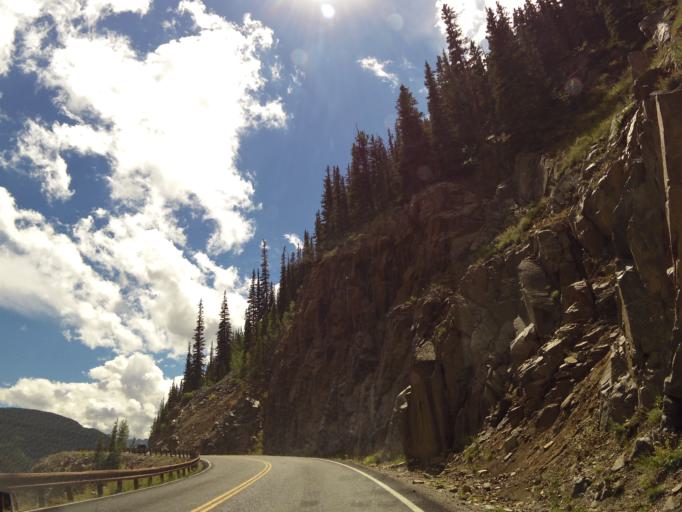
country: US
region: Colorado
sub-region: San Juan County
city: Silverton
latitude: 37.7939
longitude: -107.6735
